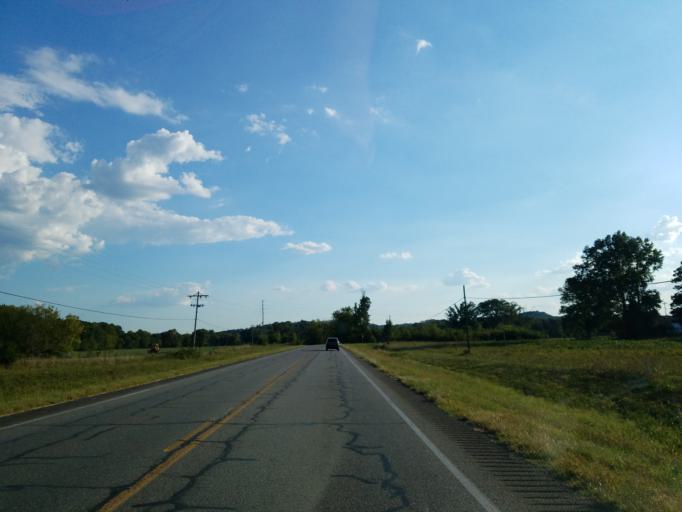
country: US
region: Georgia
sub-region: Murray County
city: Chatsworth
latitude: 34.9014
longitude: -84.7485
